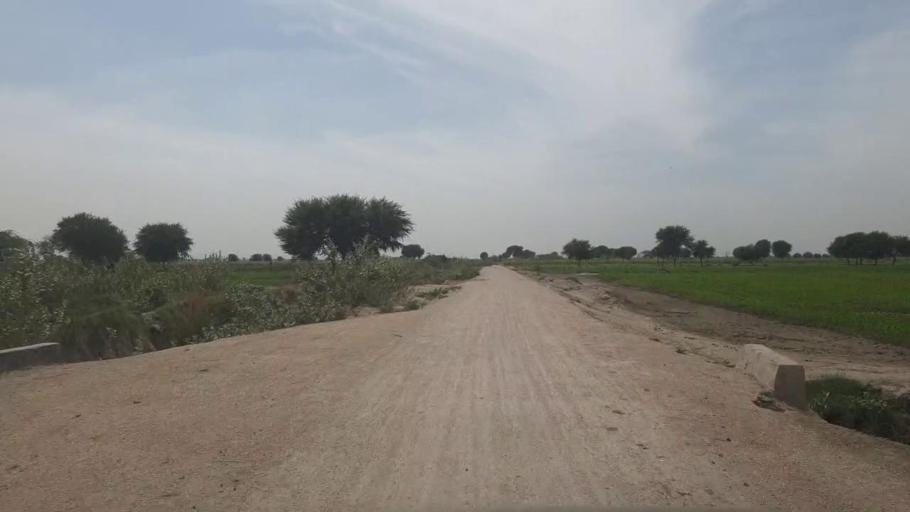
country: PK
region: Sindh
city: Kunri
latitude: 25.2244
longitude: 69.6782
